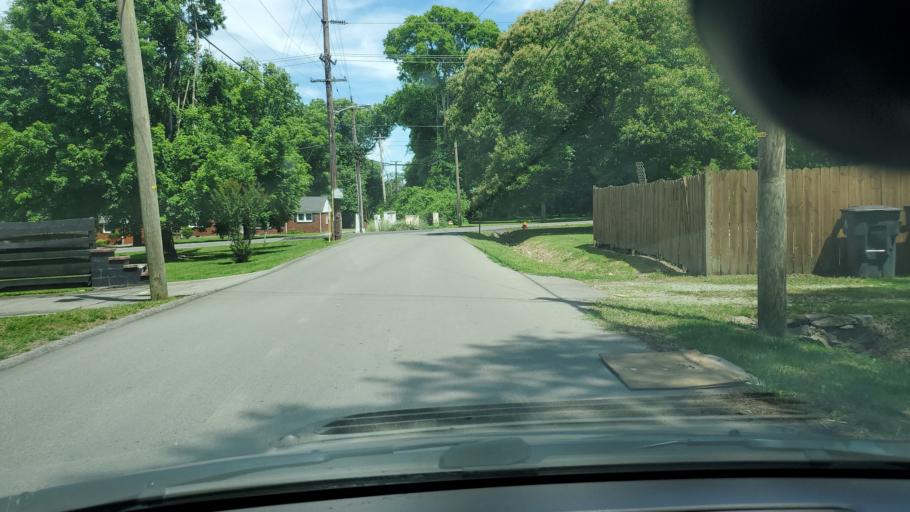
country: US
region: Tennessee
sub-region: Davidson County
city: Nashville
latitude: 36.2279
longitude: -86.7339
